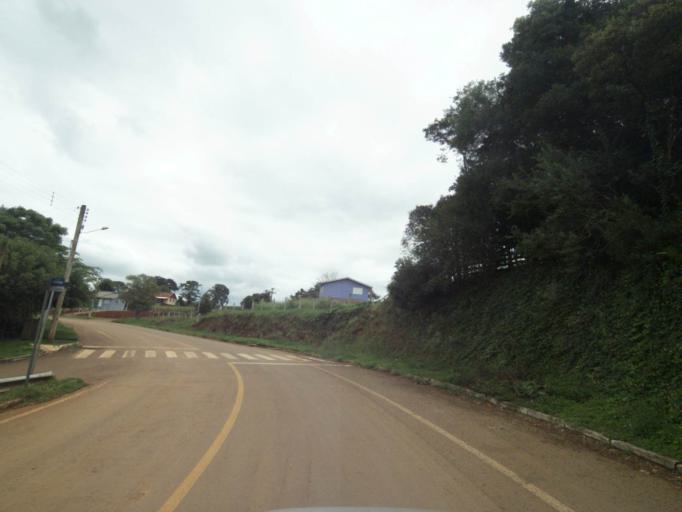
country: BR
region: Rio Grande do Sul
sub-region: Lagoa Vermelha
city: Lagoa Vermelha
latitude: -28.2118
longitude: -51.5445
